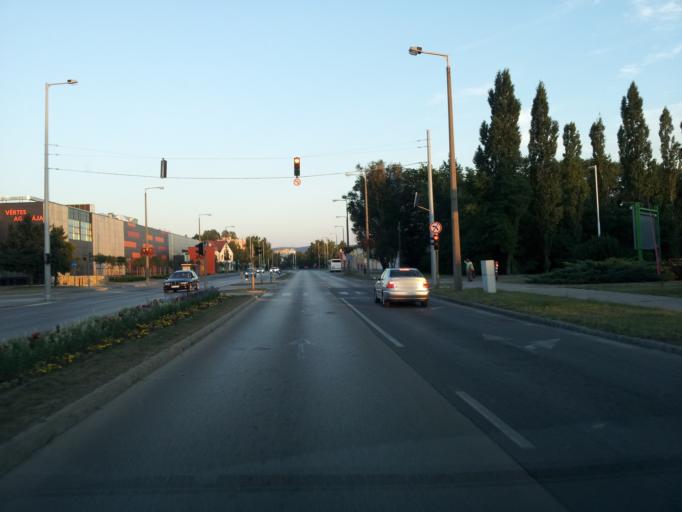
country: HU
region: Komarom-Esztergom
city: Tatabanya
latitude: 47.5823
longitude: 18.3976
